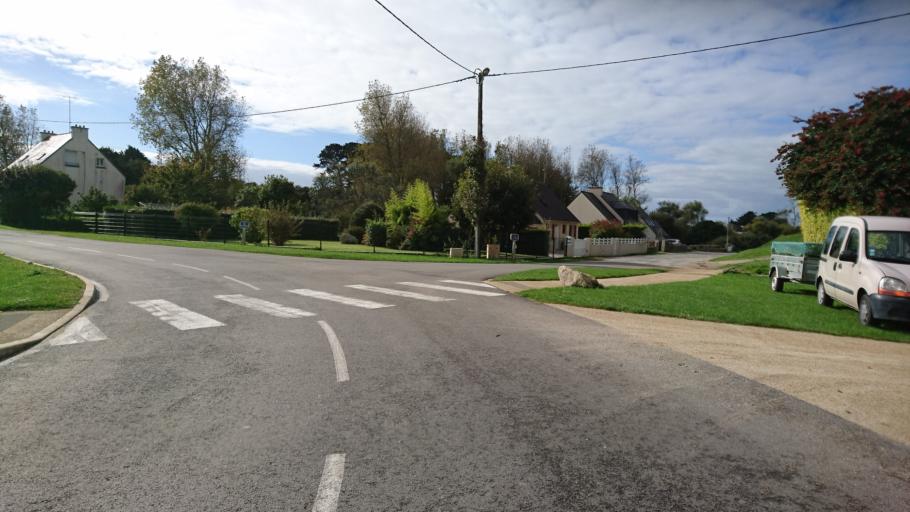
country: FR
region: Brittany
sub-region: Departement du Finistere
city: Lampaul-Plouarzel
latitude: 48.4444
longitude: -4.7701
